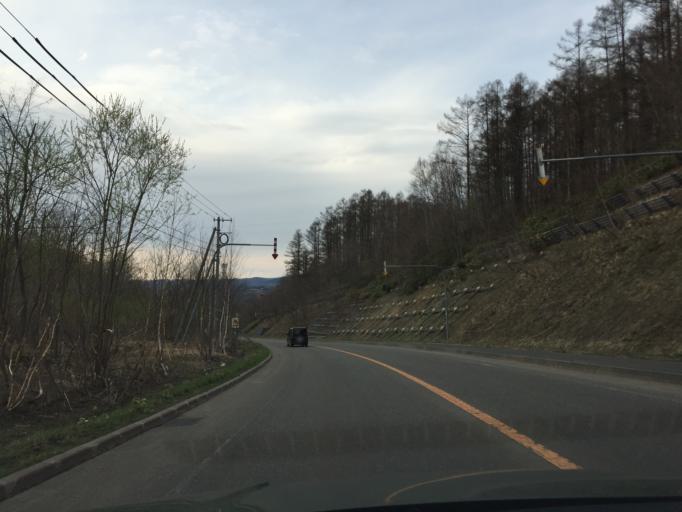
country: JP
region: Hokkaido
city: Akabira
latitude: 43.5328
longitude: 142.0679
